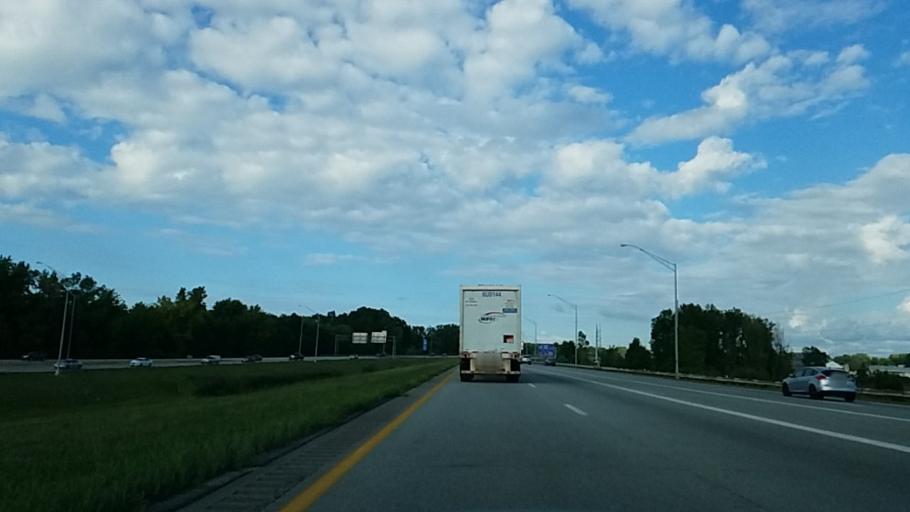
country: US
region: Ohio
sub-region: Lorain County
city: North Ridgeville
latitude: 41.3835
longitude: -81.9844
